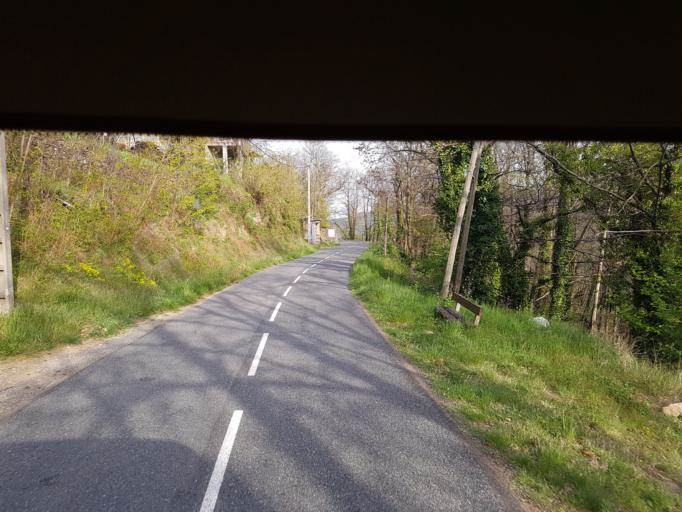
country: FR
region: Languedoc-Roussillon
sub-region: Departement du Gard
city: Branoux-les-Taillades
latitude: 44.3302
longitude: 3.8930
